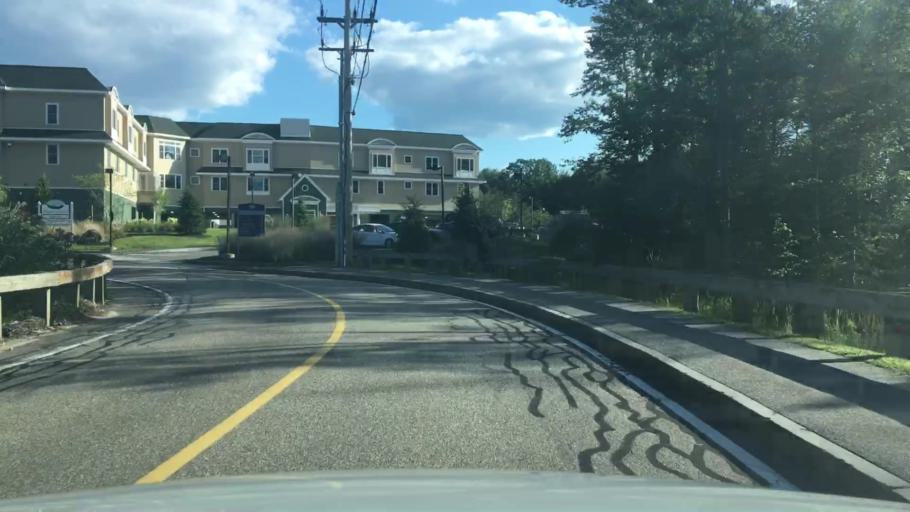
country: US
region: Maine
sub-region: Cumberland County
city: Scarborough
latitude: 43.5594
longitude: -70.2884
